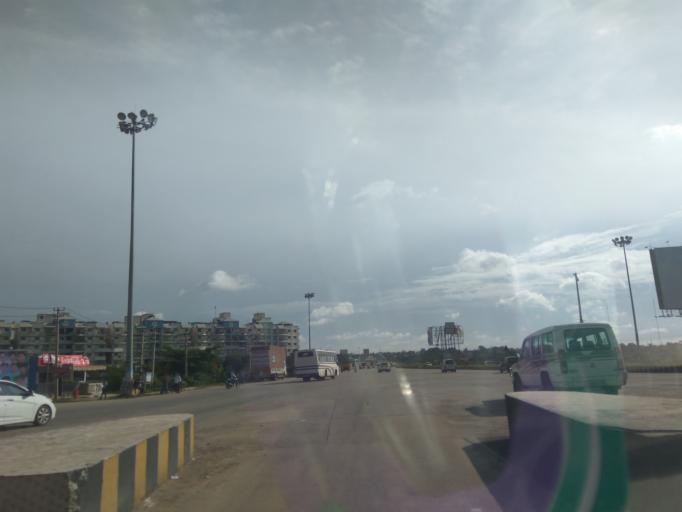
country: IN
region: Karnataka
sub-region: Bangalore Rural
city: Hoskote
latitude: 13.0596
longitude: 77.7707
